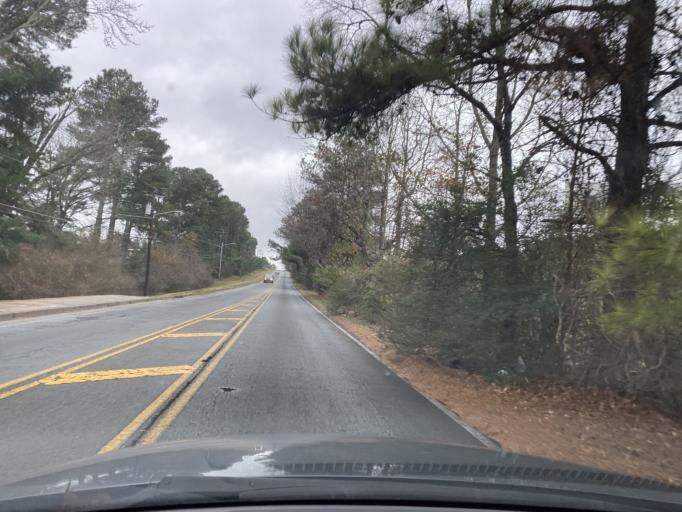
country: US
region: Georgia
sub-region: DeKalb County
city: Redan
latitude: 33.7029
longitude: -84.1604
